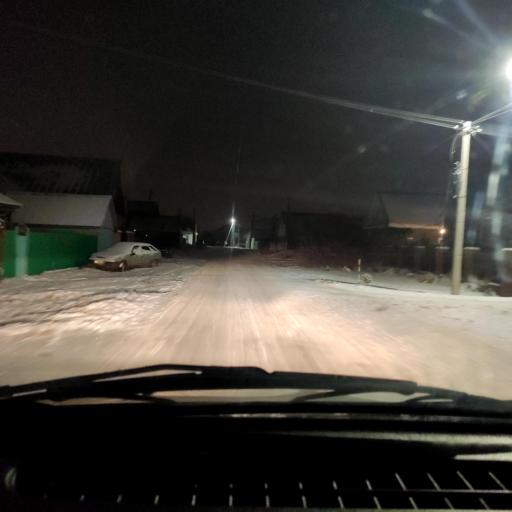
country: RU
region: Bashkortostan
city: Ufa
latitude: 54.6179
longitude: 55.9398
